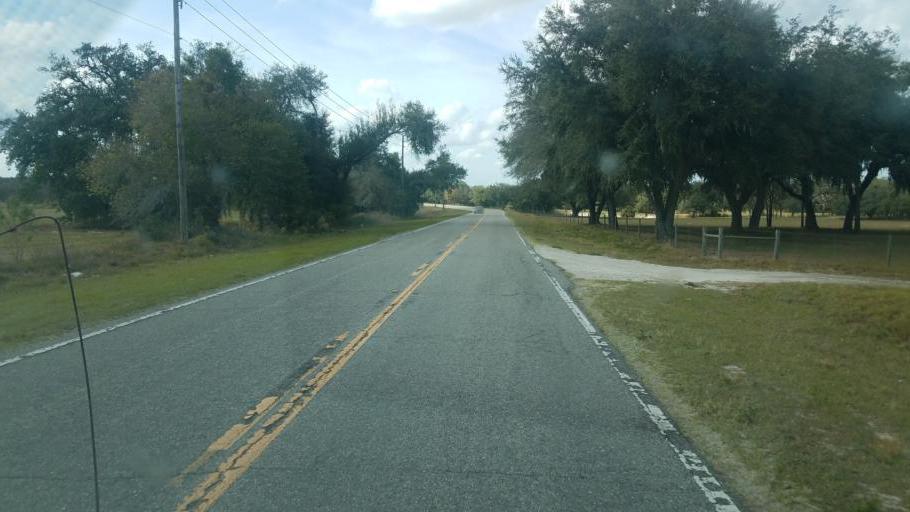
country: US
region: Florida
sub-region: Polk County
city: Haines City
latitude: 28.0830
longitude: -81.5886
